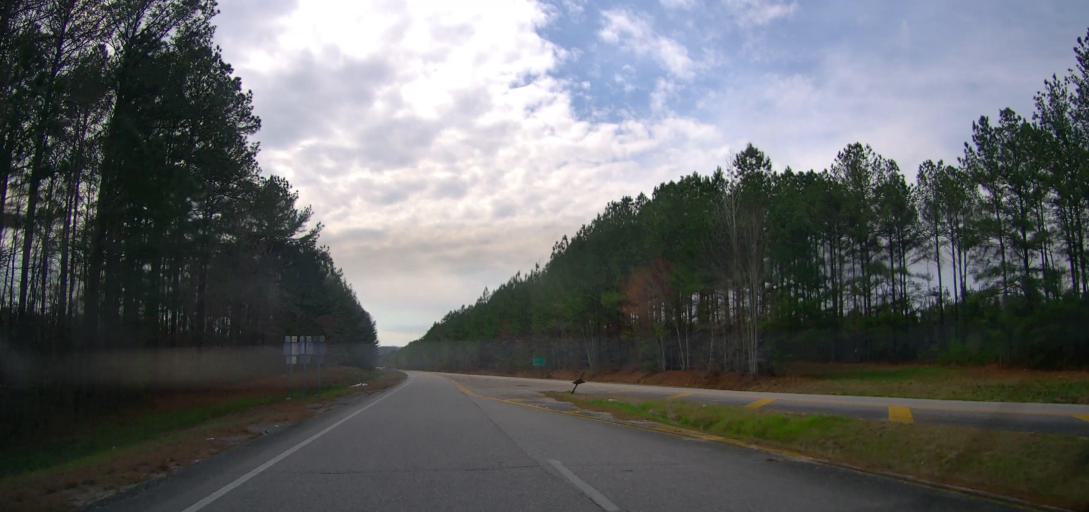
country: US
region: Alabama
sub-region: Marion County
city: Winfield
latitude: 33.9335
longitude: -87.7087
